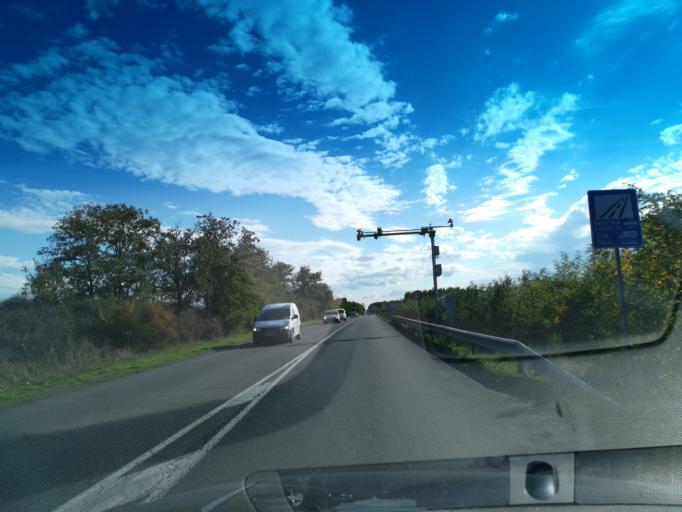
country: BG
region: Stara Zagora
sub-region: Obshtina Stara Zagora
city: Stara Zagora
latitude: 42.3598
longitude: 25.6561
